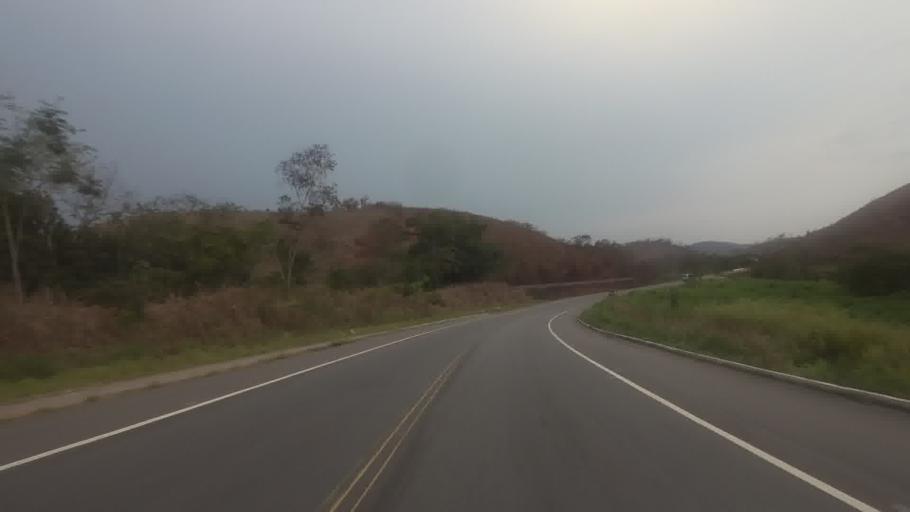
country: BR
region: Rio de Janeiro
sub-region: Carmo
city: Carmo
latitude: -21.8253
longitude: -42.6063
